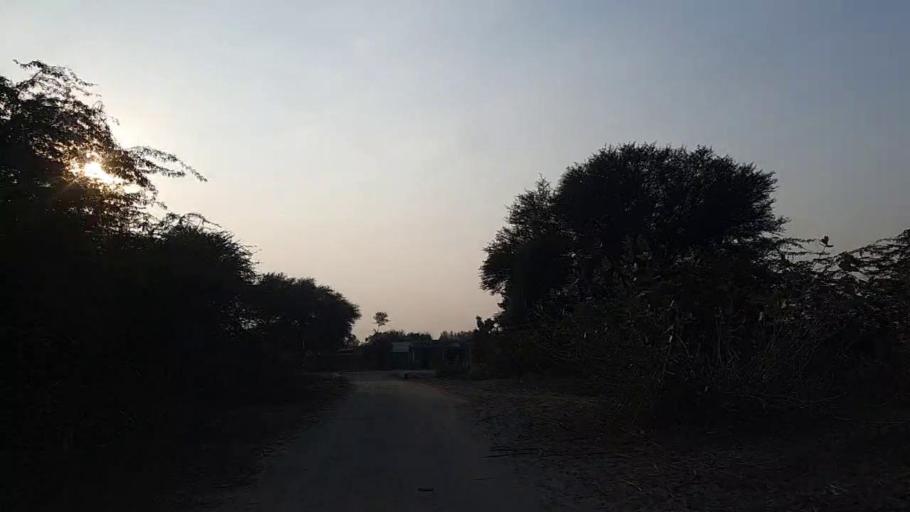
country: PK
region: Sindh
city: Jam Sahib
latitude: 26.4301
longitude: 68.5842
